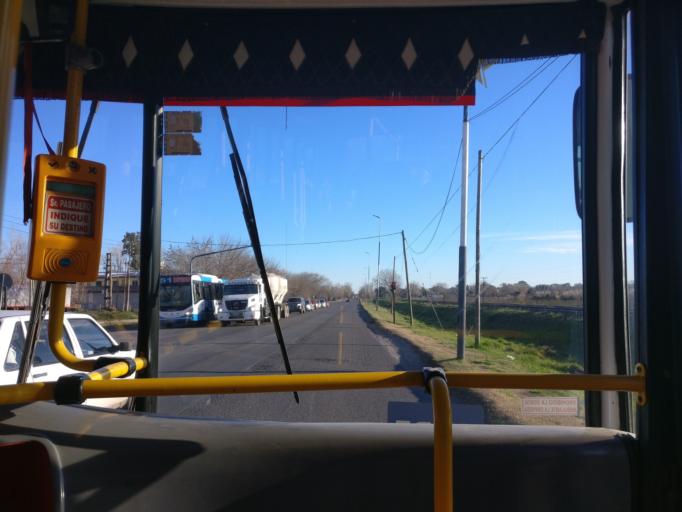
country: AR
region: Buenos Aires
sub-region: Partido de Ezeiza
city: Ezeiza
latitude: -34.9043
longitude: -58.5866
